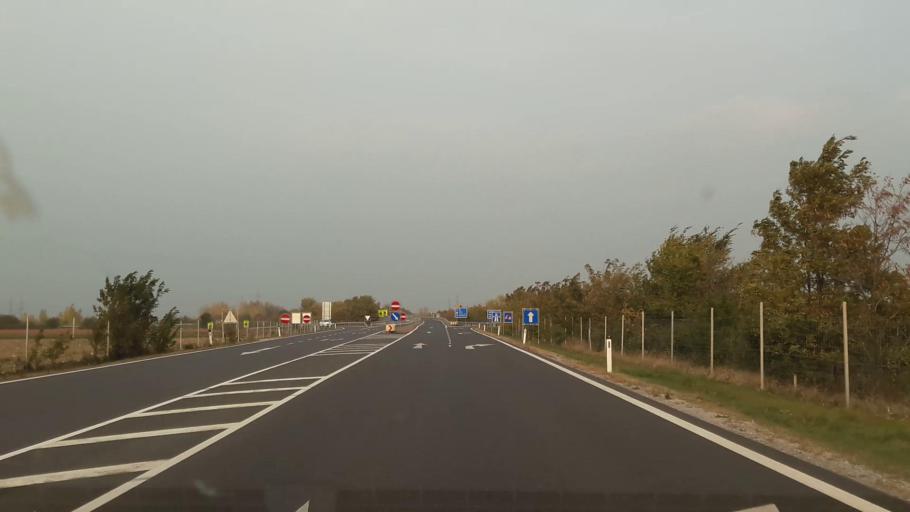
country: AT
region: Burgenland
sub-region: Politischer Bezirk Neusiedl am See
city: Gols
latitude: 47.9448
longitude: 16.9311
